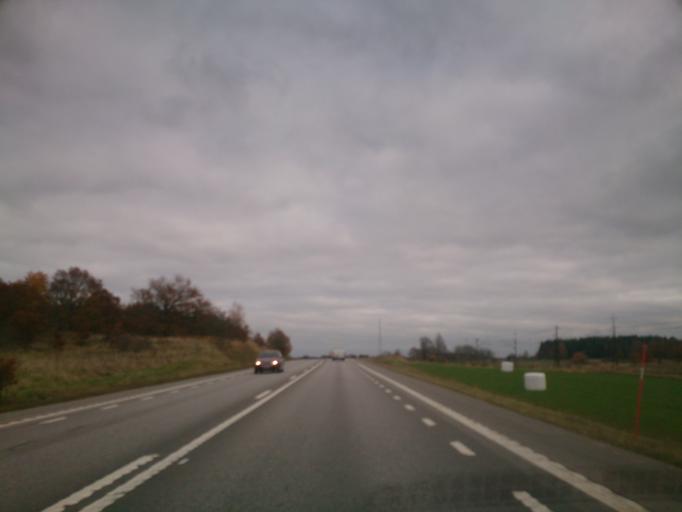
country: SE
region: OEstergoetland
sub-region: Linkopings Kommun
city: Linghem
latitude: 58.4590
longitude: 15.8650
